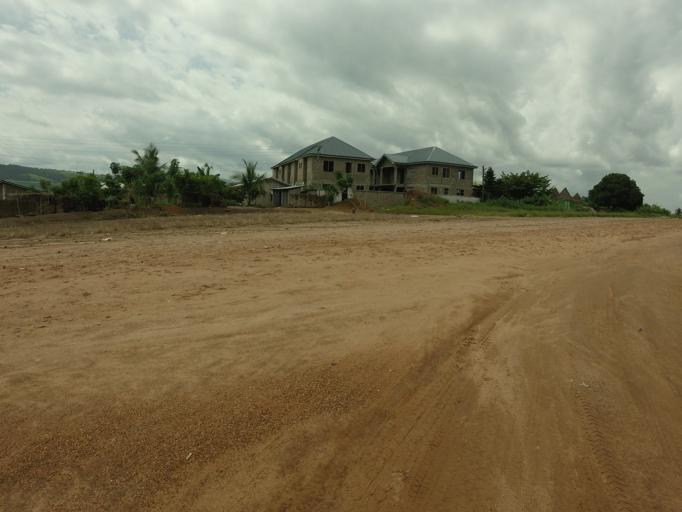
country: GH
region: Volta
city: Ho
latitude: 6.5834
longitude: 0.4584
